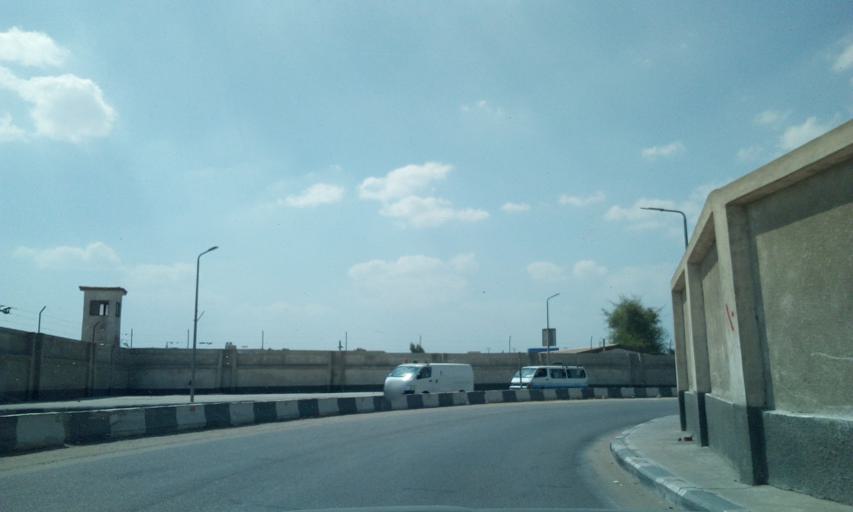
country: EG
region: Muhafazat al Qahirah
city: Cairo
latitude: 30.0783
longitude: 31.3610
